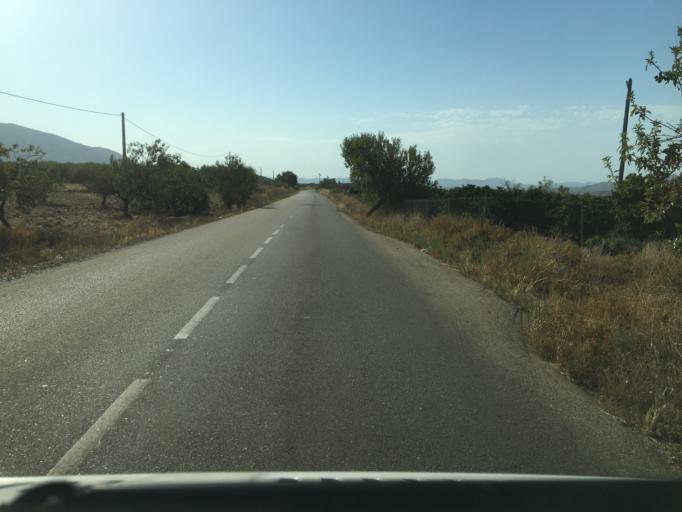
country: ES
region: Andalusia
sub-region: Provincia de Almeria
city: Huercal-Overa
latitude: 37.4687
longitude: -1.8908
